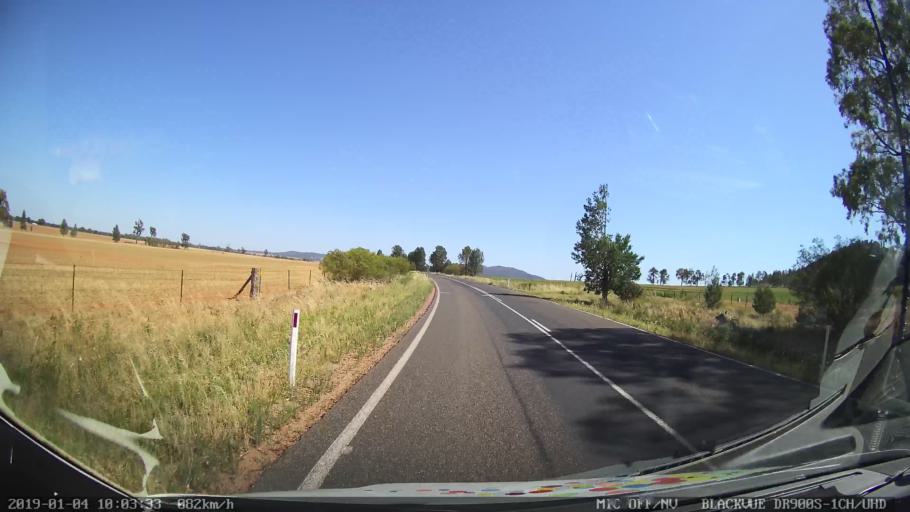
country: AU
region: New South Wales
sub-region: Cabonne
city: Canowindra
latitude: -33.4625
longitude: 148.3643
